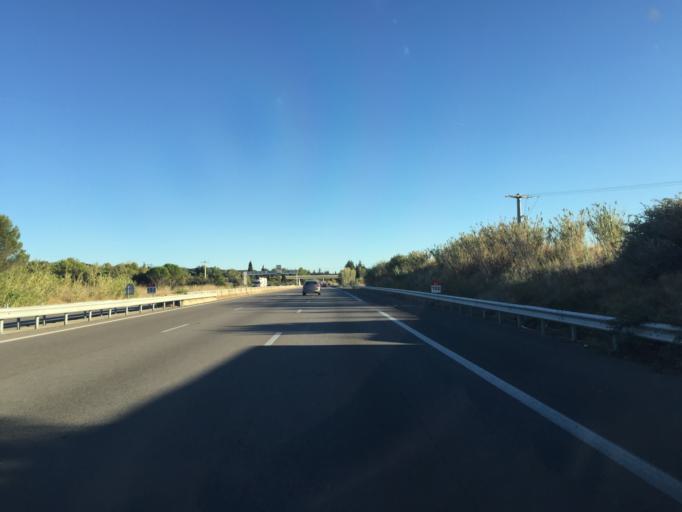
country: FR
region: Provence-Alpes-Cote d'Azur
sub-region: Departement du Vaucluse
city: Morieres-les-Avignon
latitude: 43.9515
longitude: 4.9081
